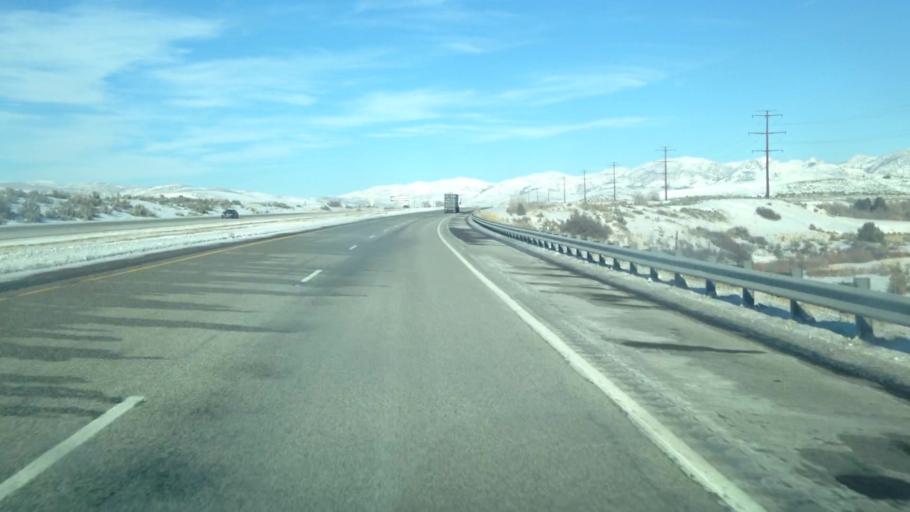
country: US
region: Idaho
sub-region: Oneida County
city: Malad City
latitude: 42.2244
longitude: -112.2373
